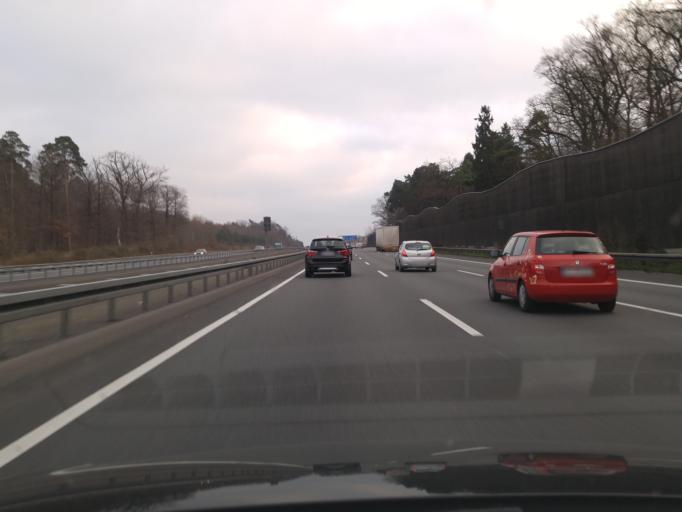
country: DE
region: Lower Saxony
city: Helmstedt
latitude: 52.2295
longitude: 11.0321
